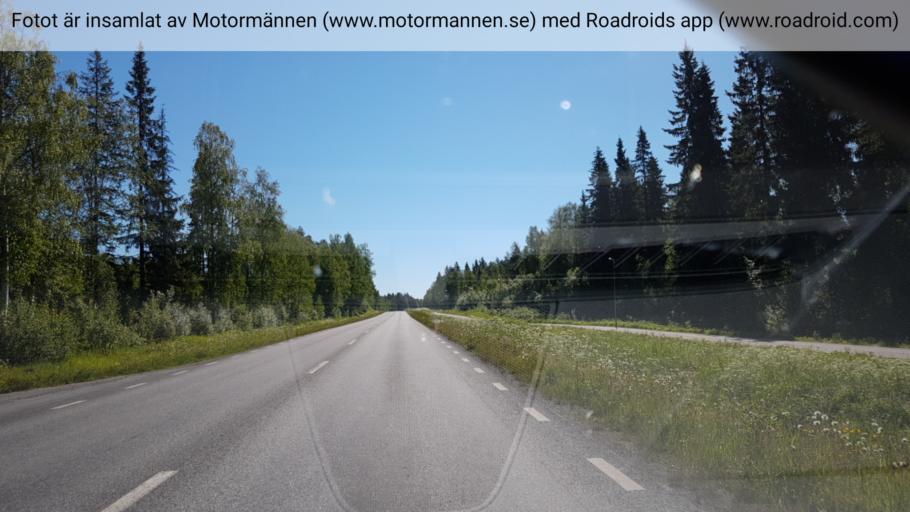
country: SE
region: Norrbotten
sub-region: Bodens Kommun
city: Boden
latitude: 65.8329
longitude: 21.6171
